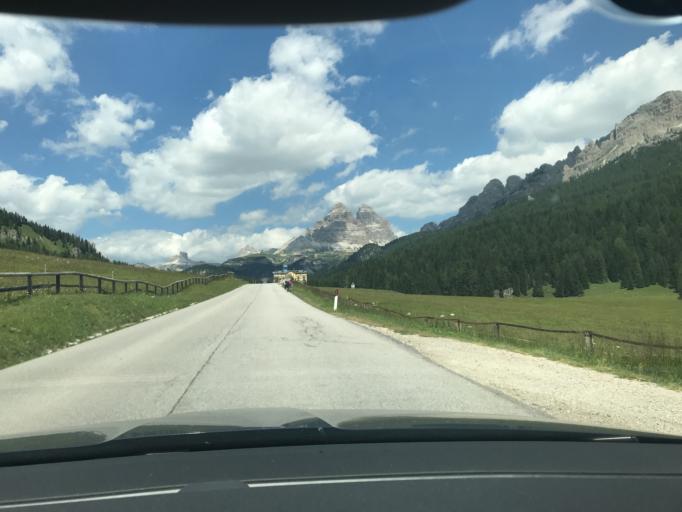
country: IT
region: Veneto
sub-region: Provincia di Belluno
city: Cortina d'Ampezzo
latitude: 46.5720
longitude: 12.2470
